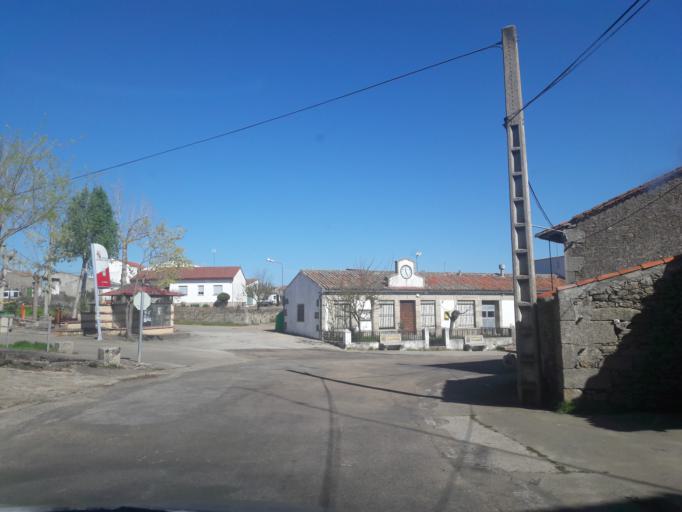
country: ES
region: Castille and Leon
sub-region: Provincia de Salamanca
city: Valsalabroso
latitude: 41.1523
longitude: -6.4876
